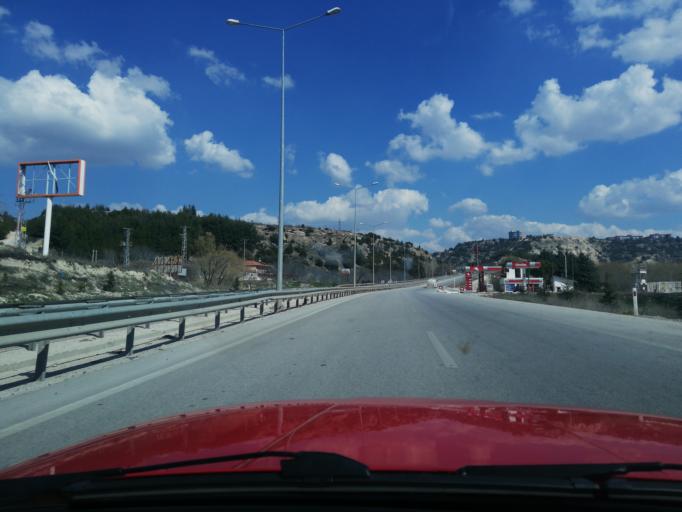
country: TR
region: Burdur
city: Burdur
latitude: 37.6988
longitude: 30.3238
